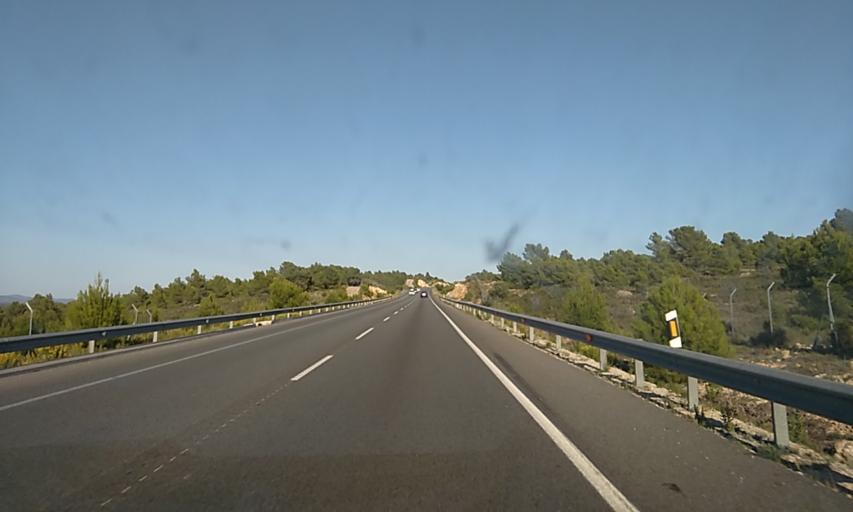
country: ES
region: Valencia
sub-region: Provincia de Castello
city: Torreblanca
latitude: 40.2175
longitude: 0.1579
